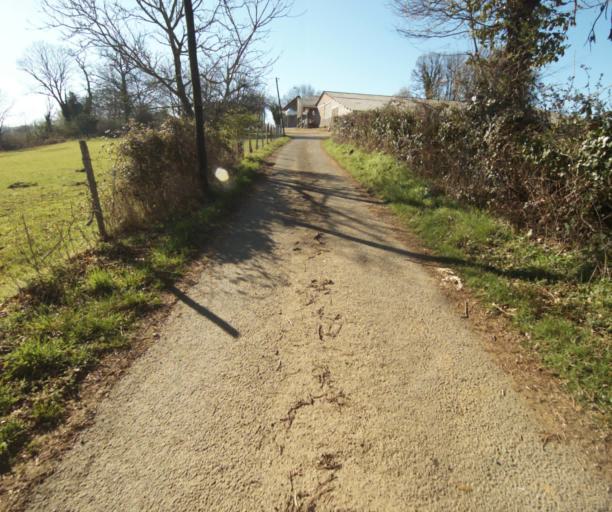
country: FR
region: Limousin
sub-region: Departement de la Correze
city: Chamboulive
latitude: 45.4208
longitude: 1.6819
